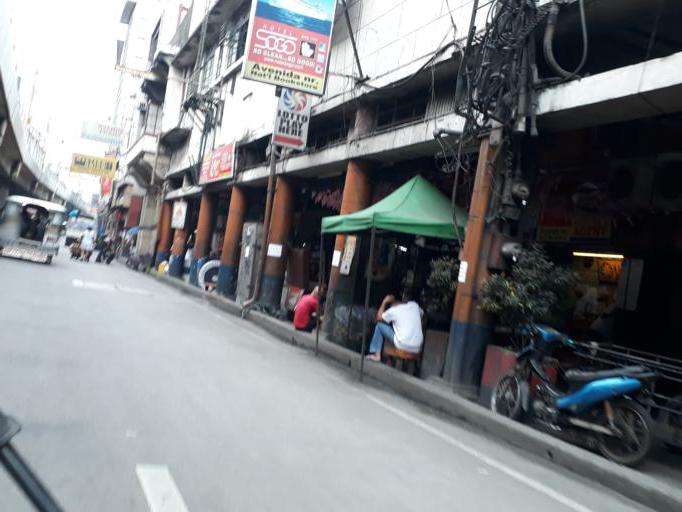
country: PH
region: Metro Manila
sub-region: City of Manila
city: Manila
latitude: 14.6034
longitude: 120.9820
